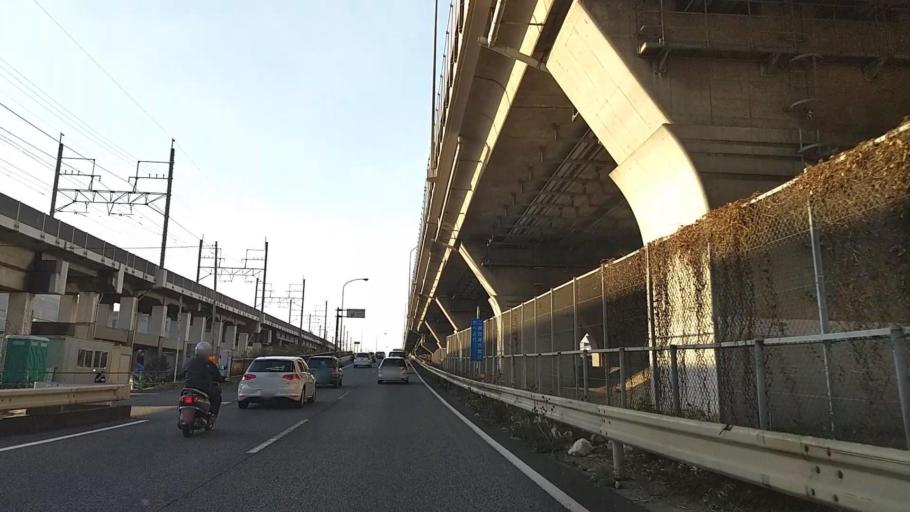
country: JP
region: Chiba
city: Funabashi
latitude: 35.6896
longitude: 139.9719
